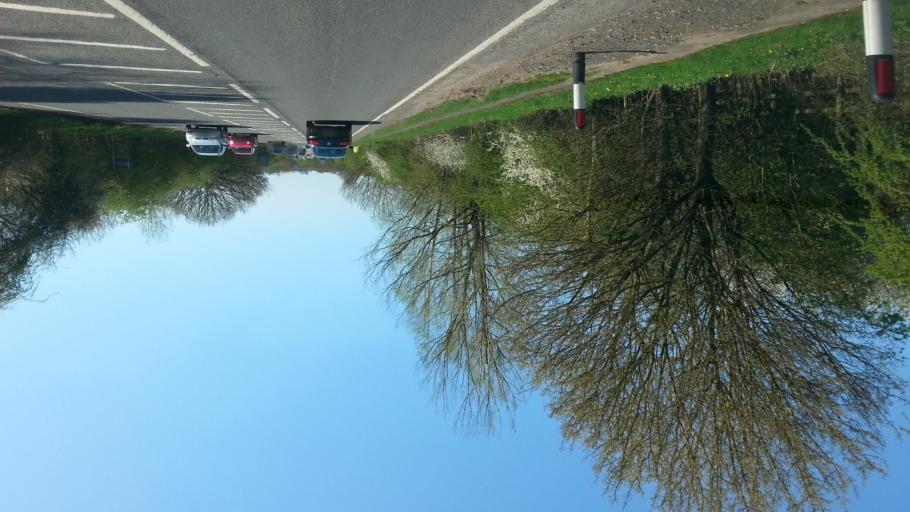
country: GB
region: England
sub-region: Worcestershire
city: Alvechurch
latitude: 52.3680
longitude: -1.9541
